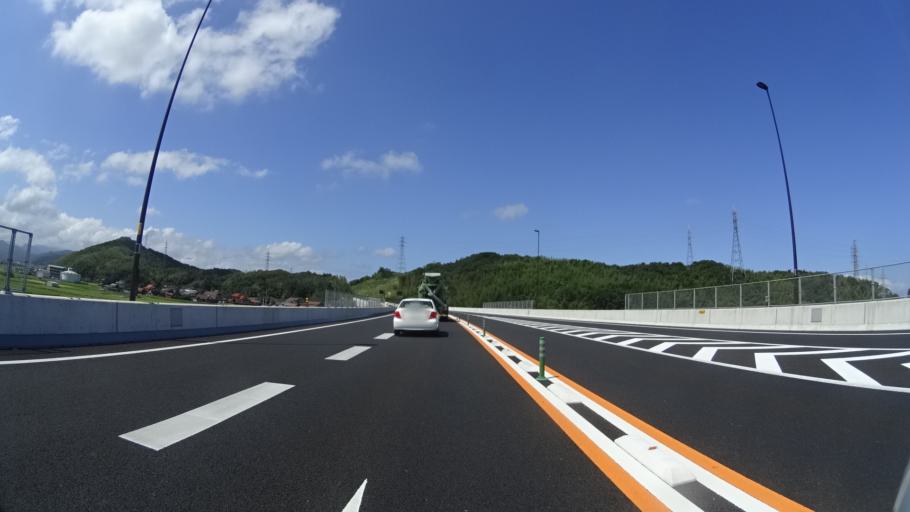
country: JP
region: Tottori
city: Tottori
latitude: 35.4946
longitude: 134.1885
